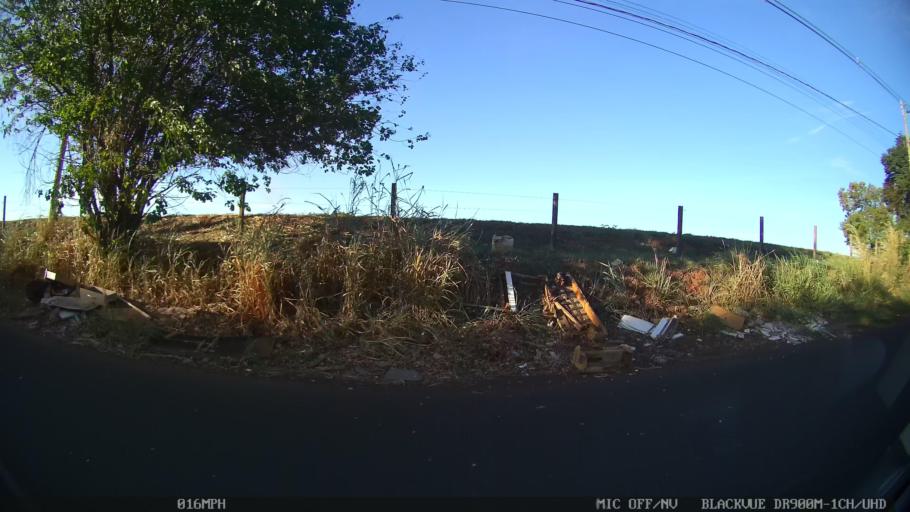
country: BR
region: Sao Paulo
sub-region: Sao Jose Do Rio Preto
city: Sao Jose do Rio Preto
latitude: -20.8667
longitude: -49.3303
